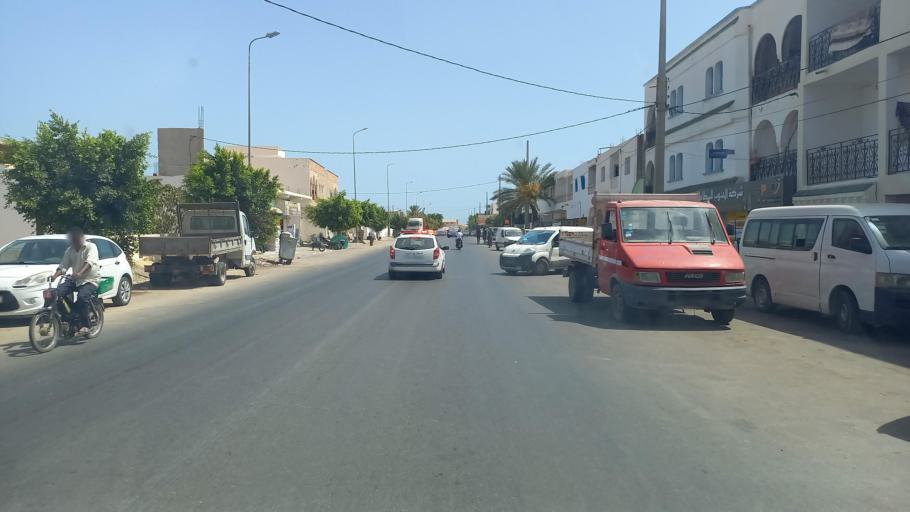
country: TN
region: Madanin
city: Zarzis
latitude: 33.4967
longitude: 11.0885
